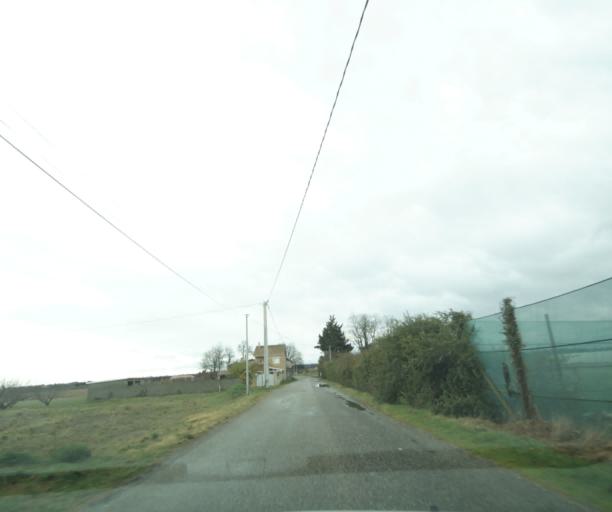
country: FR
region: Rhone-Alpes
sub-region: Departement de la Drome
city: Bourg-les-Valence
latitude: 44.9591
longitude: 4.9142
